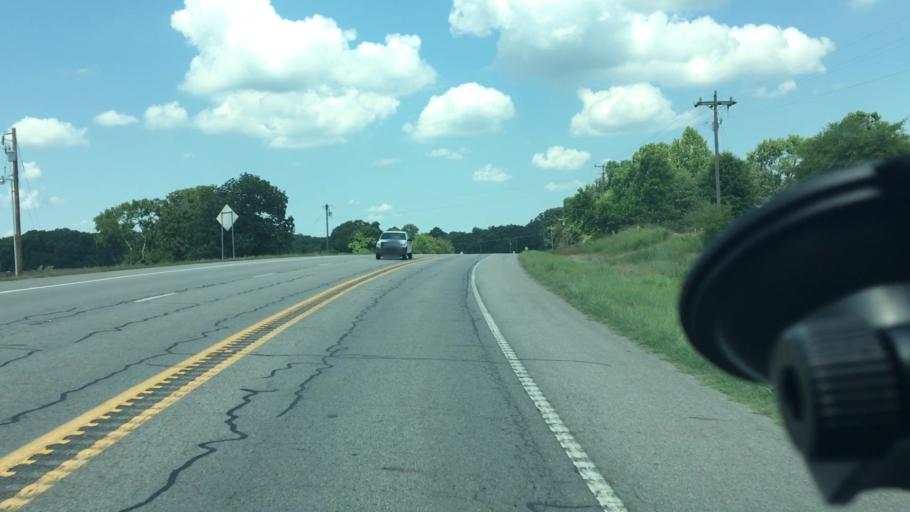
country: US
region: Arkansas
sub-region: Logan County
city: Paris
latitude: 35.2989
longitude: -93.8279
